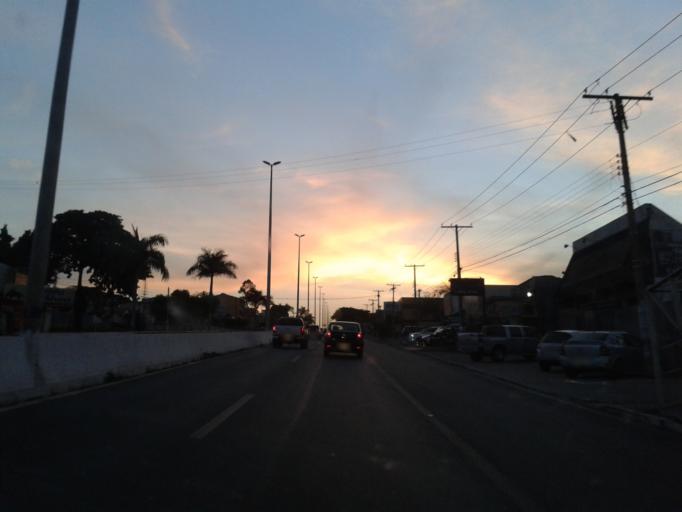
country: BR
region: Goias
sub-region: Goiania
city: Goiania
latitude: -16.6601
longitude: -49.3329
